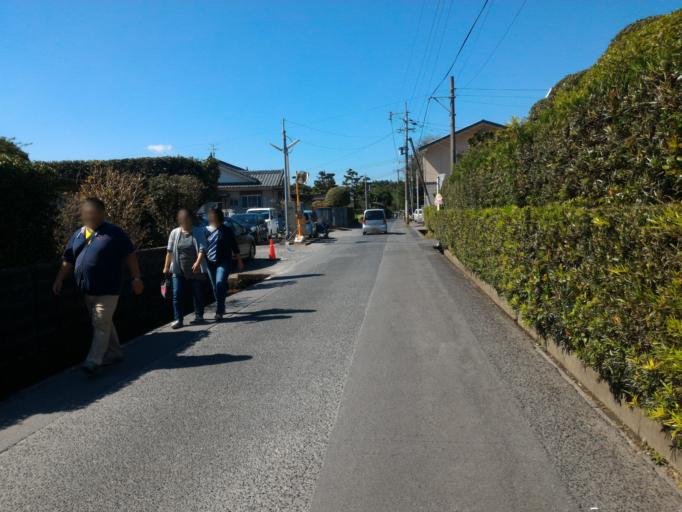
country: JP
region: Kagoshima
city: Kanoya
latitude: 31.3439
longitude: 130.9458
